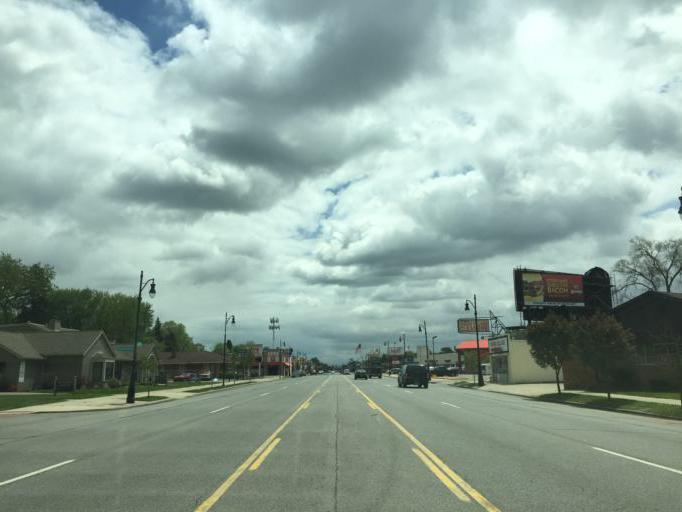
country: US
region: Michigan
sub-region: Oakland County
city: Southfield
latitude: 42.4035
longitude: -83.2253
